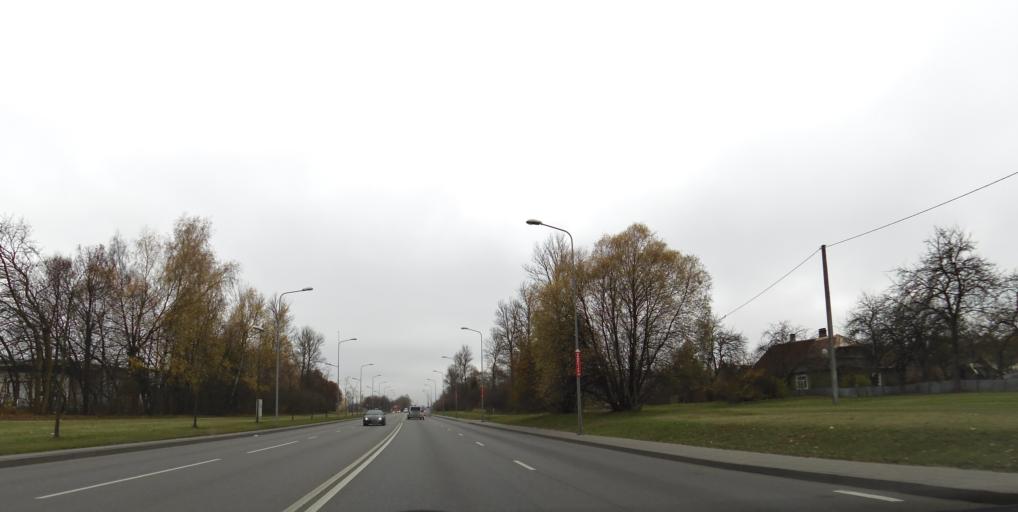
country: LT
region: Vilnius County
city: Vilkpede
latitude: 54.6491
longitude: 25.2678
